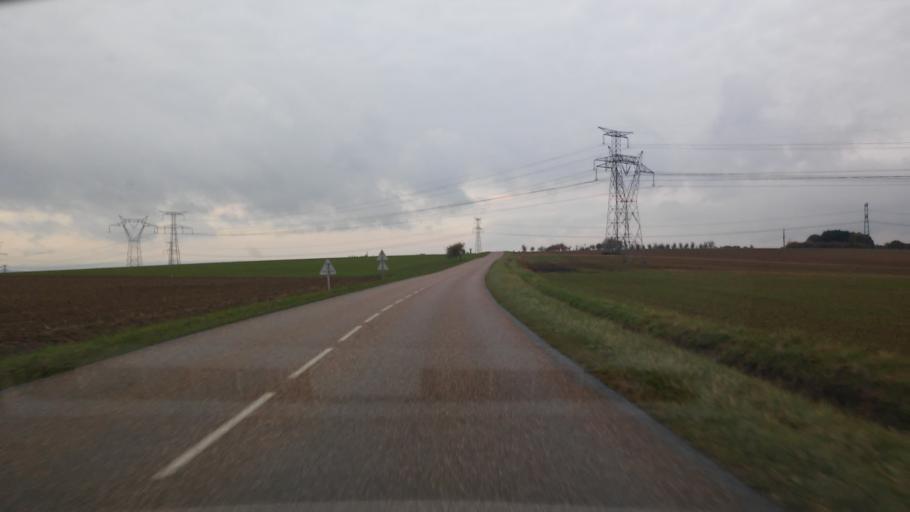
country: FR
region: Lorraine
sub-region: Departement de la Moselle
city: Vigy
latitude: 49.1863
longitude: 6.3073
